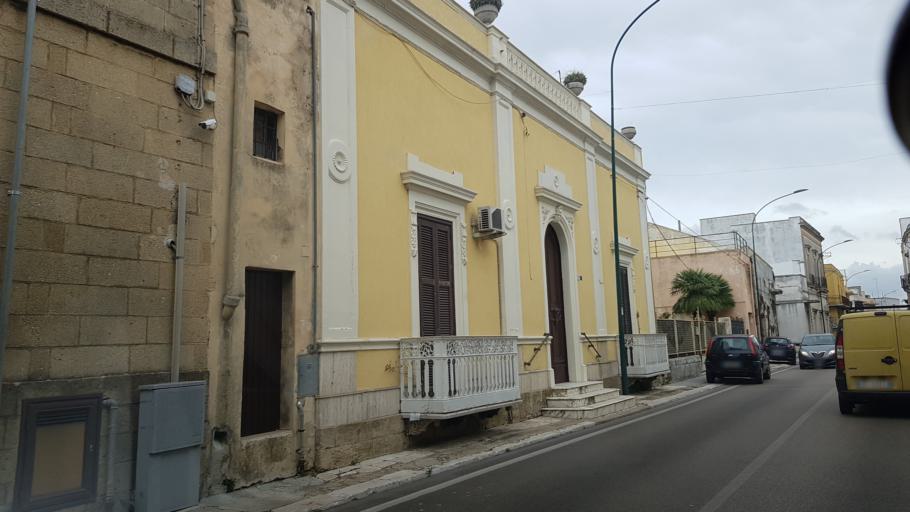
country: IT
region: Apulia
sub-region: Provincia di Lecce
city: Guagnano
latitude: 40.4012
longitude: 17.9504
